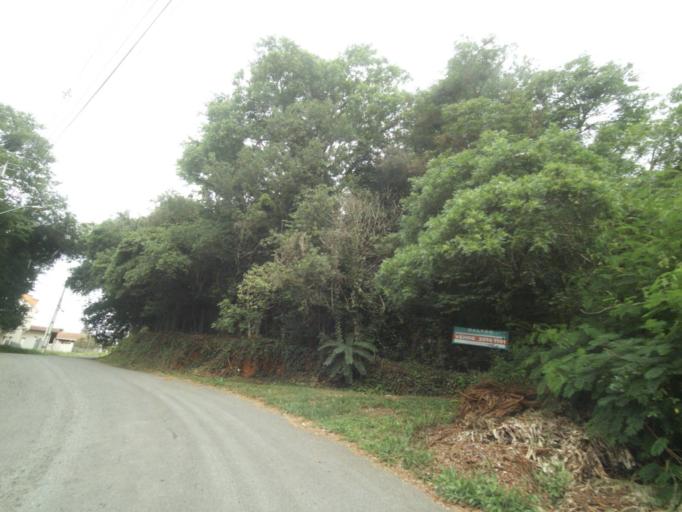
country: BR
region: Parana
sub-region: Curitiba
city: Curitiba
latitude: -25.4039
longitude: -49.2974
